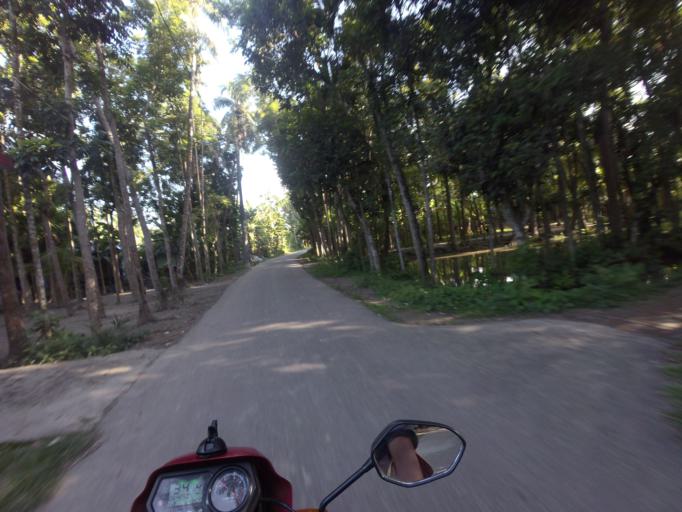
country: BD
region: Khulna
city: Bhatpara Abhaynagar
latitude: 22.9238
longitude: 89.5183
